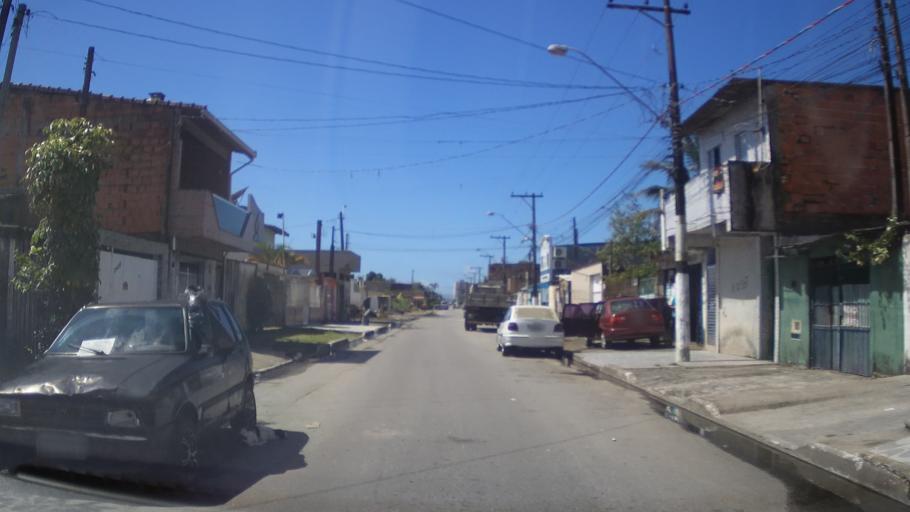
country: BR
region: Sao Paulo
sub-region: Mongagua
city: Mongagua
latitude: -24.0364
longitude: -46.5309
